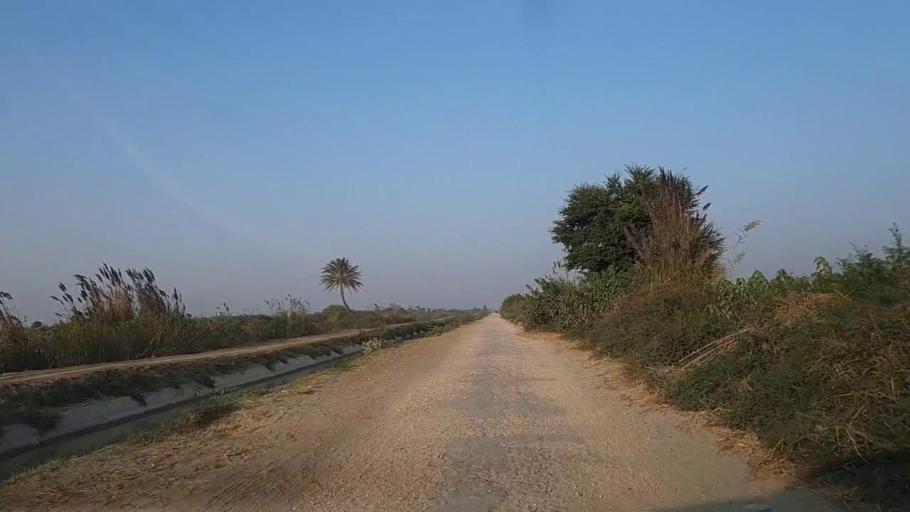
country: PK
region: Sindh
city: Keti Bandar
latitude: 24.2784
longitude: 67.6855
